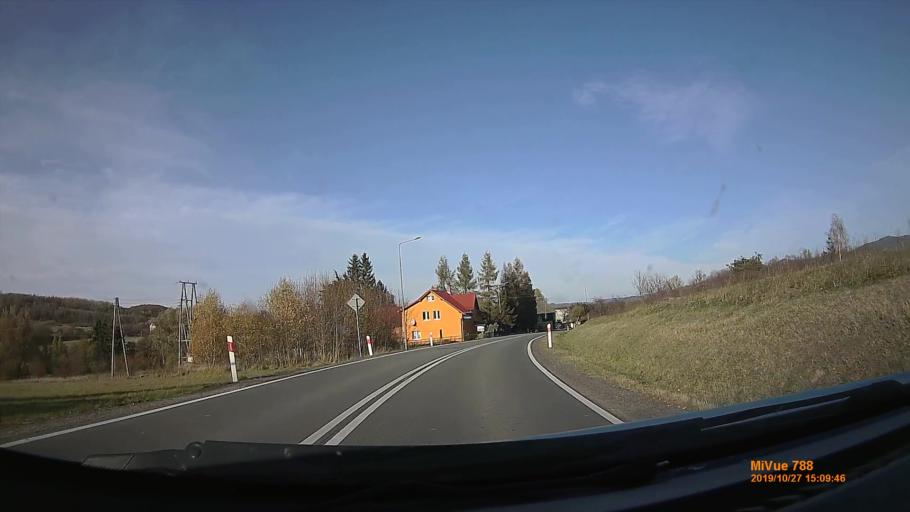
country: PL
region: Lower Silesian Voivodeship
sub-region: Powiat klodzki
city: Miedzylesie
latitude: 50.1825
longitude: 16.6683
